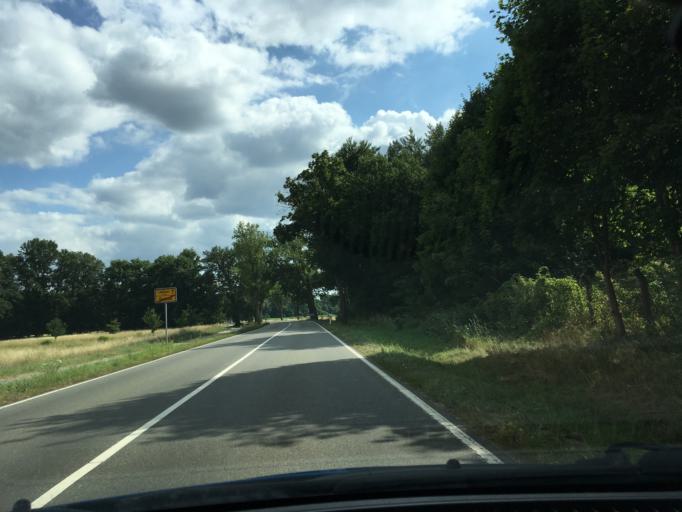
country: DE
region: Mecklenburg-Vorpommern
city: Lubtheen
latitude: 53.3313
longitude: 11.0755
